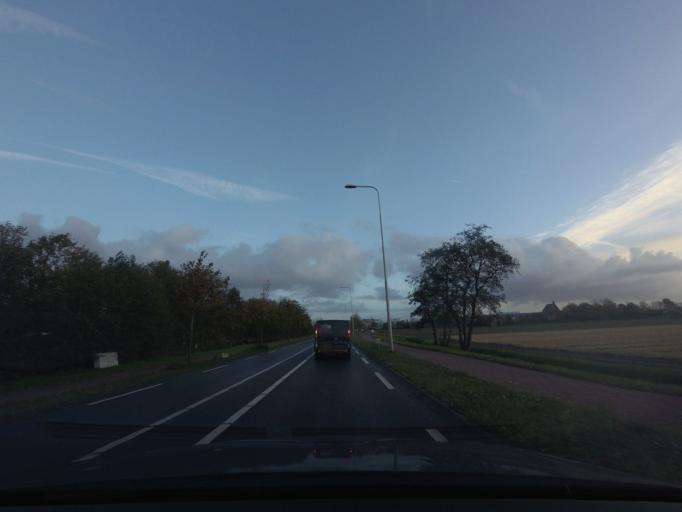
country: NL
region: South Holland
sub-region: Gemeente Lisse
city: Lisse
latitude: 52.2477
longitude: 4.5433
